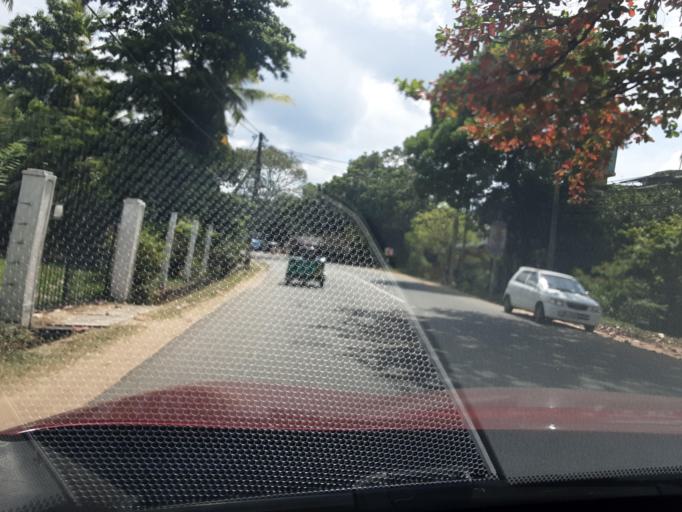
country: LK
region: North Western
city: Kurunegala
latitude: 7.4742
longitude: 80.3306
